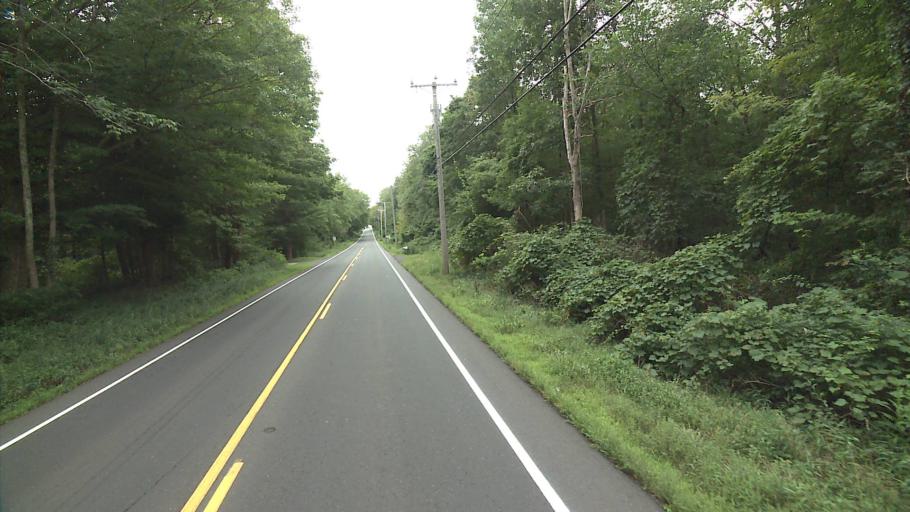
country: US
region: Connecticut
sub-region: New London County
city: Colchester
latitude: 41.5393
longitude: -72.3031
